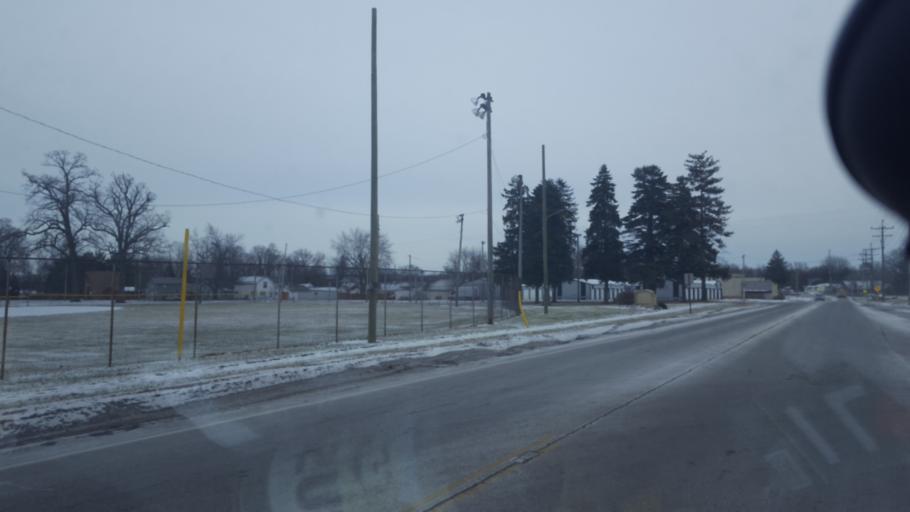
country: US
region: Ohio
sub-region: Marion County
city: Marion
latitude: 40.5899
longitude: -83.0965
